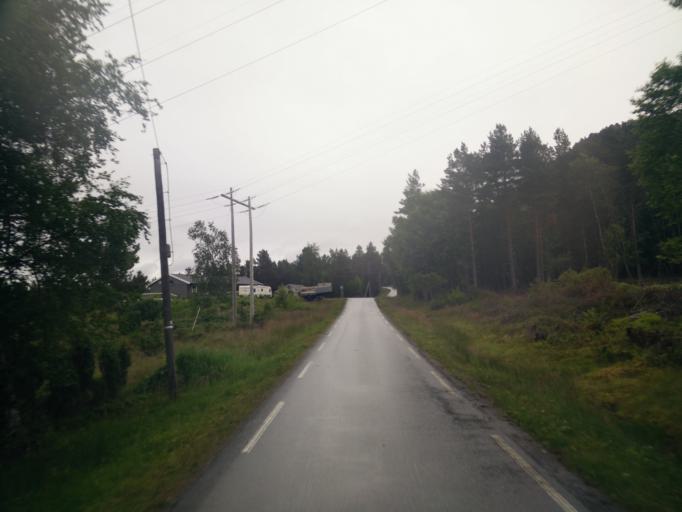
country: NO
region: More og Romsdal
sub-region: Kristiansund
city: Rensvik
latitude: 63.0230
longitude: 7.8968
